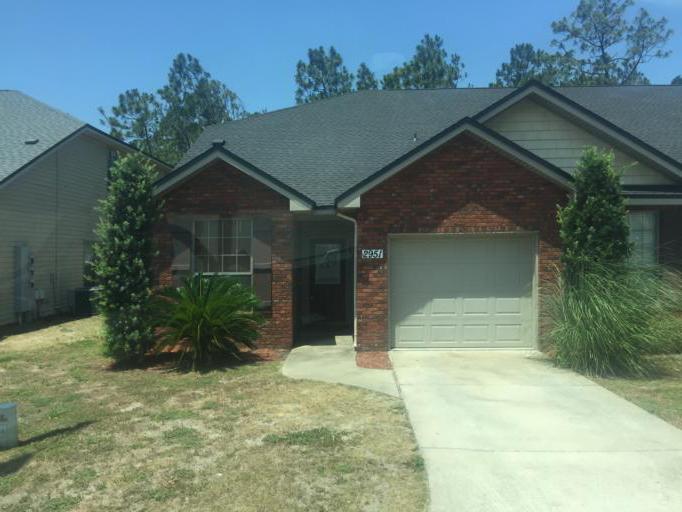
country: US
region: Florida
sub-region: Bay County
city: Hiland Park
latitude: 30.2136
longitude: -85.6534
